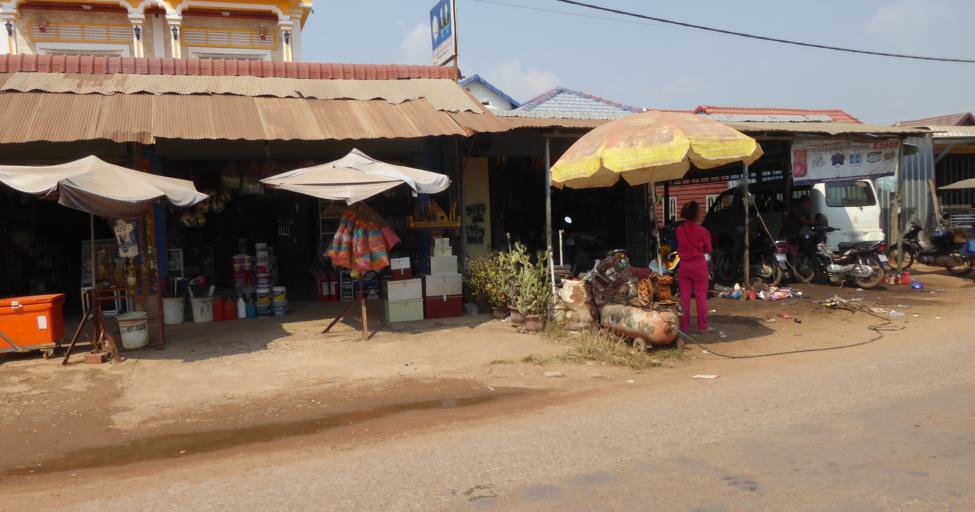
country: KH
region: Siem Reap
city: Siem Reap
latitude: 13.2866
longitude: 103.8203
